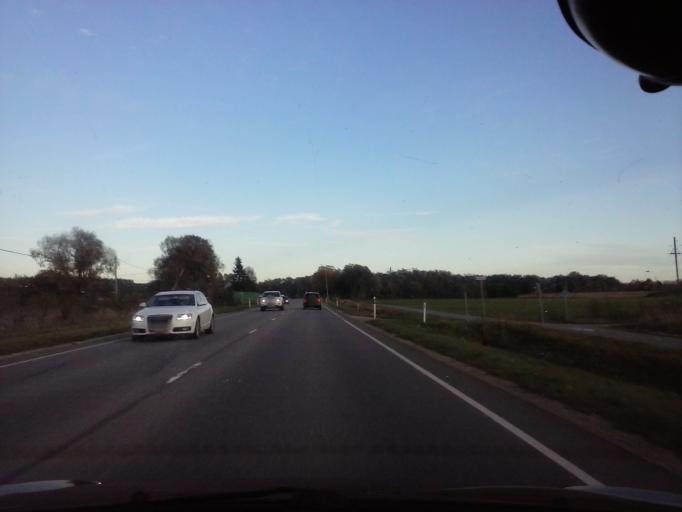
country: EE
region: Laeaene
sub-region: Ridala Parish
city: Uuemoisa
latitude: 58.9716
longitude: 23.8702
